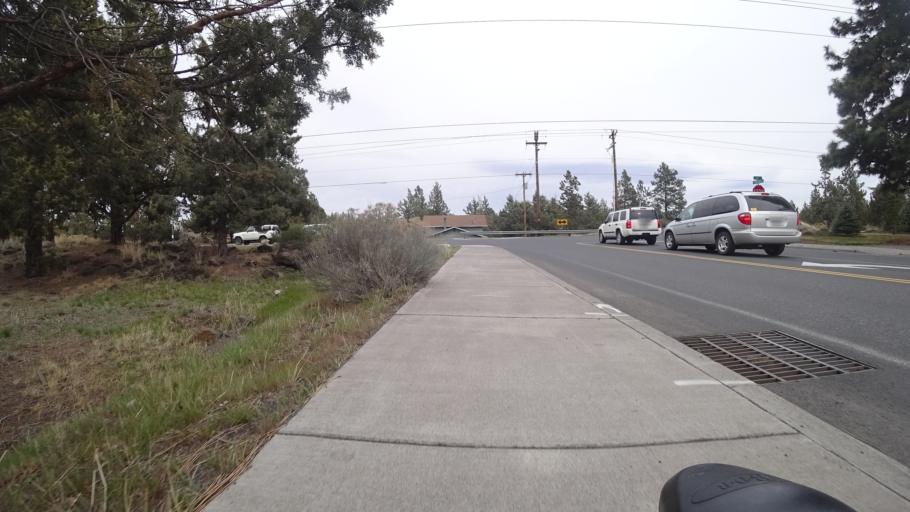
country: US
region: Oregon
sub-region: Deschutes County
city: Bend
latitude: 44.0443
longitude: -121.2842
